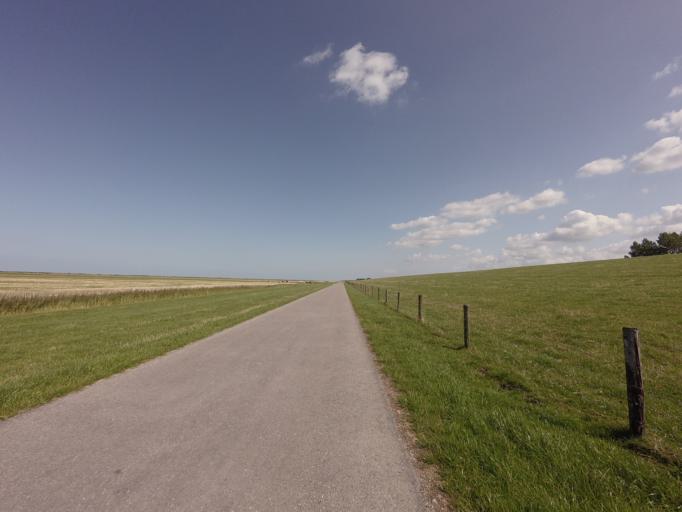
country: NL
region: Friesland
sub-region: Gemeente Ferwerderadiel
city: Marrum
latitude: 53.3417
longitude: 5.7910
